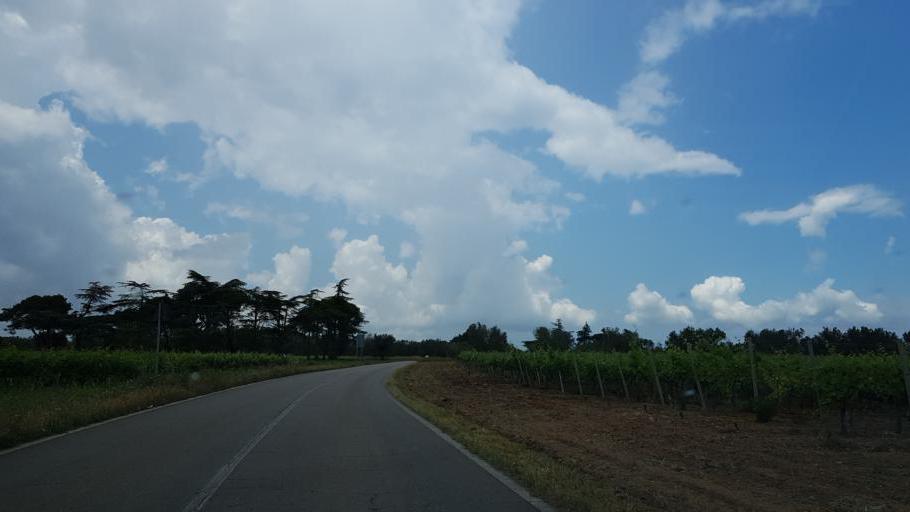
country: IT
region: Apulia
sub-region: Provincia di Brindisi
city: San Donaci
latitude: 40.4688
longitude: 17.9301
